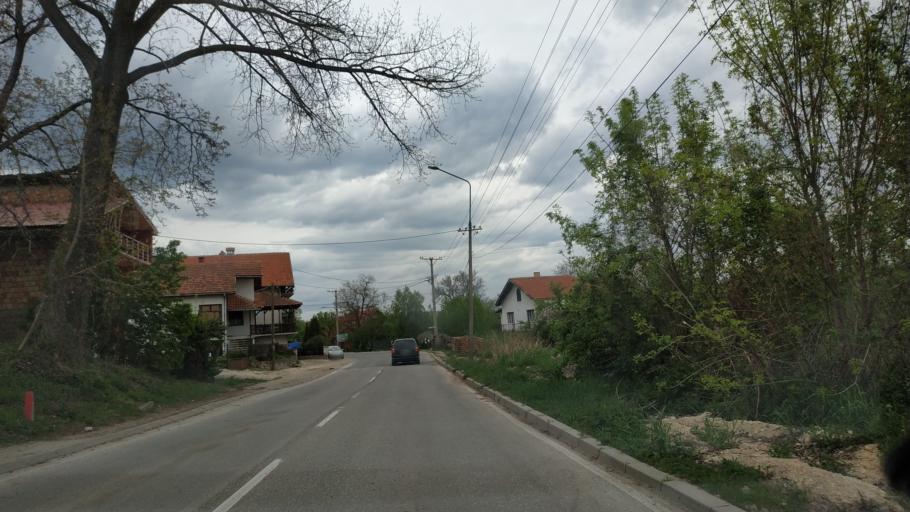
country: RS
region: Central Serbia
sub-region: Zajecarski Okrug
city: Soko Banja
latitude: 43.6498
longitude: 21.8583
